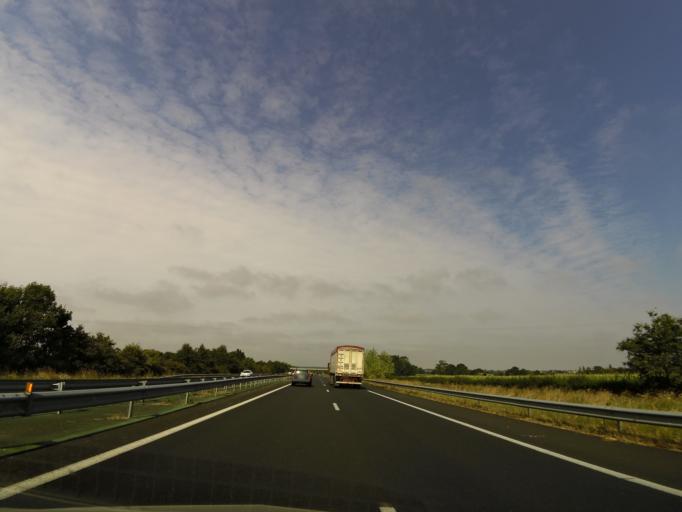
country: FR
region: Pays de la Loire
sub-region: Departement de la Vendee
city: Chauche
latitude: 46.8432
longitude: -1.2488
